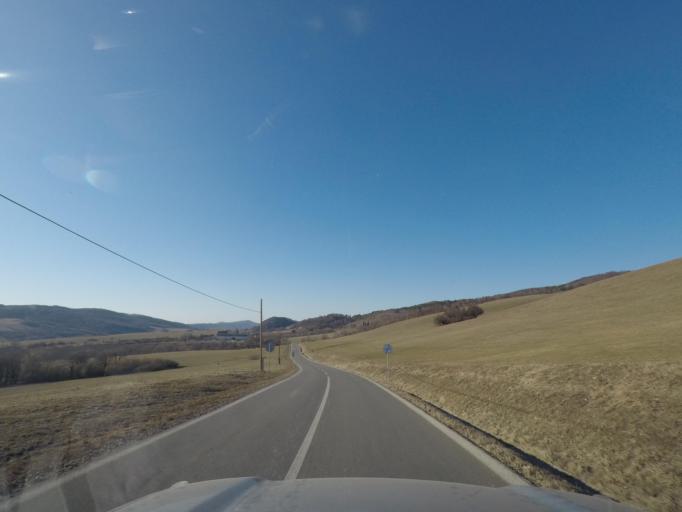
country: SK
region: Presovsky
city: Medzilaborce
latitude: 49.2159
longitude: 21.9837
